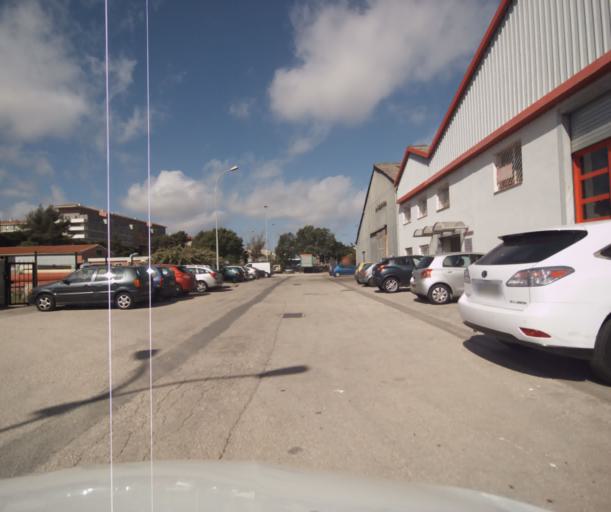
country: FR
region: Provence-Alpes-Cote d'Azur
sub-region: Departement du Var
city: La Seyne-sur-Mer
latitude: 43.1147
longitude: 5.8776
